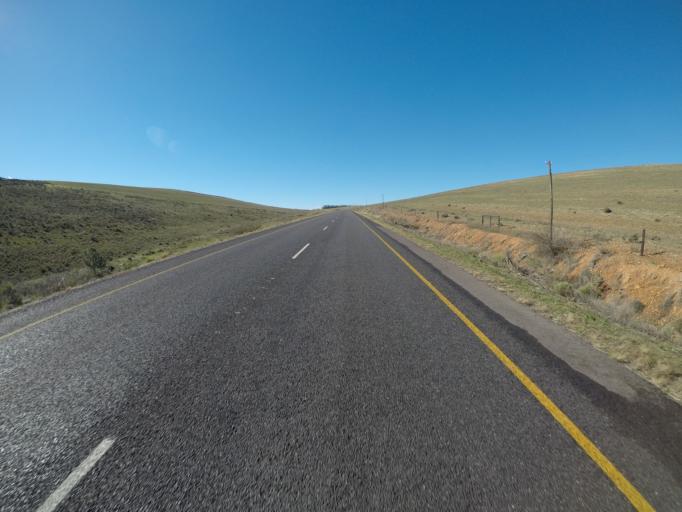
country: ZA
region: Western Cape
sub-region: Overberg District Municipality
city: Caledon
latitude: -34.1466
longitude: 19.4908
